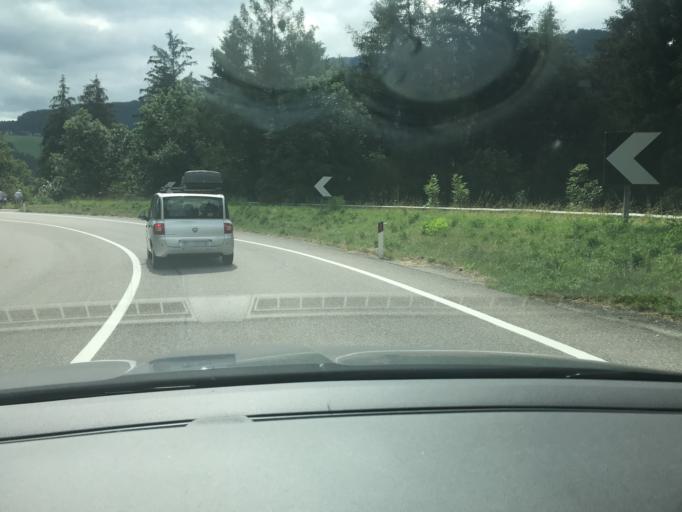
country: IT
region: Trentino-Alto Adige
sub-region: Bolzano
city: Rasun Anterselva - Rasen-Antholz
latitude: 46.7613
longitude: 12.0511
